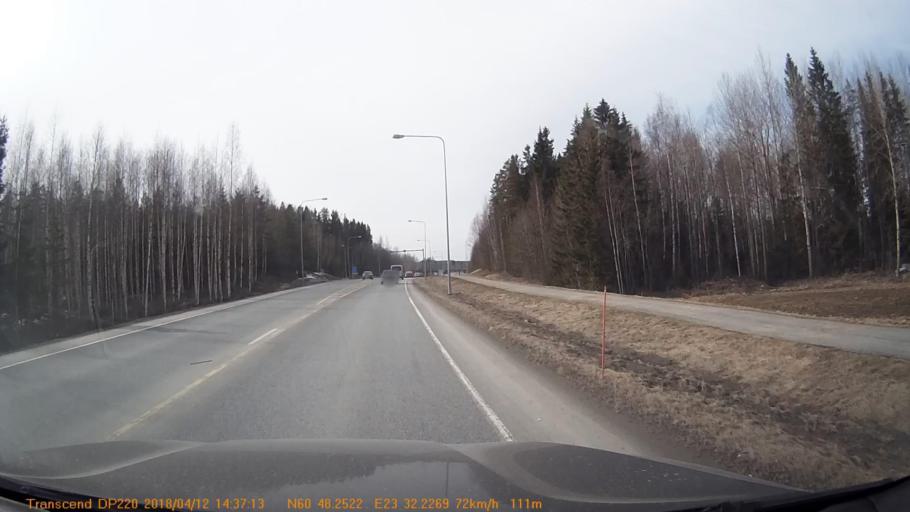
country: FI
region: Haeme
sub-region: Forssa
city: Jokioinen
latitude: 60.8047
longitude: 23.5348
